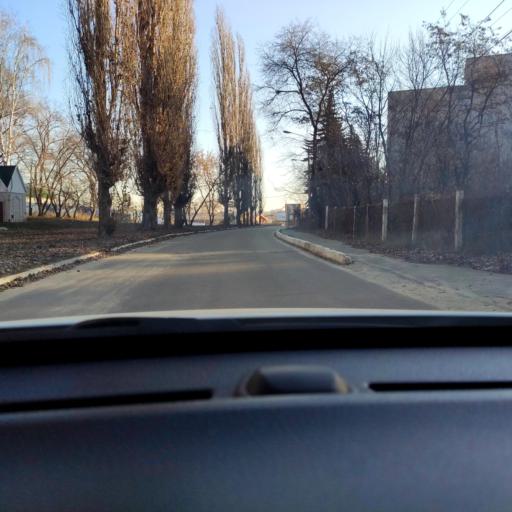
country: RU
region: Voronezj
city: Voronezh
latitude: 51.7262
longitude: 39.2324
